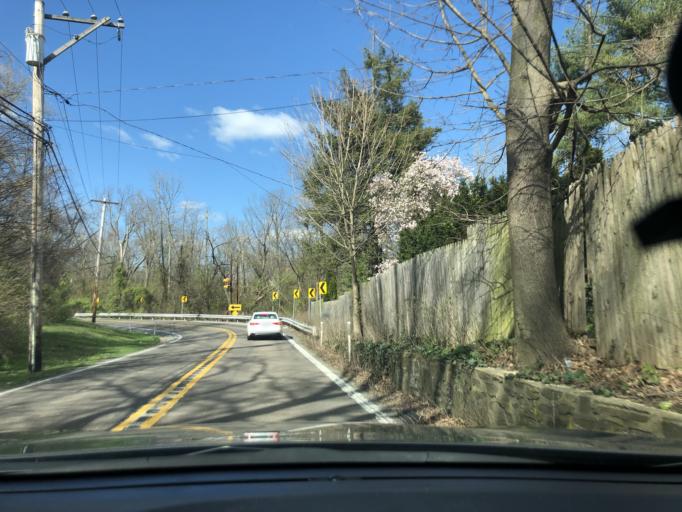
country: US
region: Pennsylvania
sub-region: Montgomery County
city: Blue Bell
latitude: 40.1389
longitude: -75.2709
